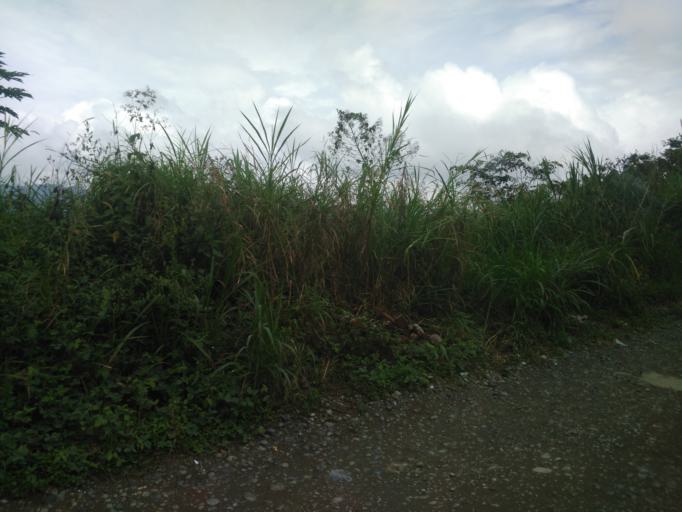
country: CO
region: Valle del Cauca
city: Sevilla
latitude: 4.2931
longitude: -75.9003
